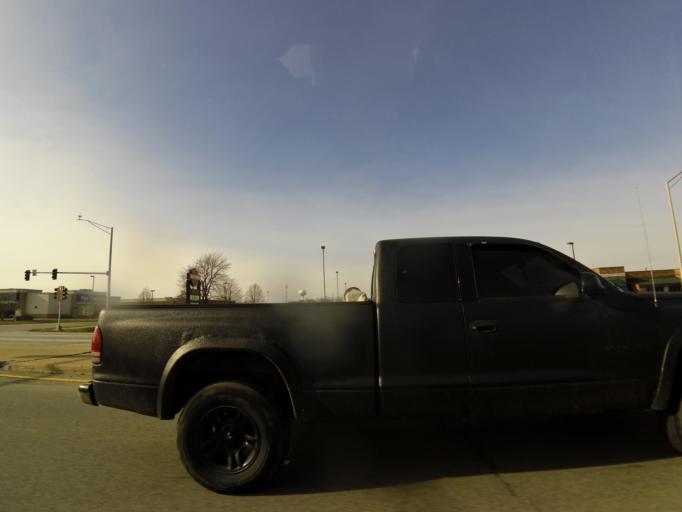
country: US
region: Illinois
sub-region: Macon County
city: Forsyth
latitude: 39.9219
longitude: -88.9554
